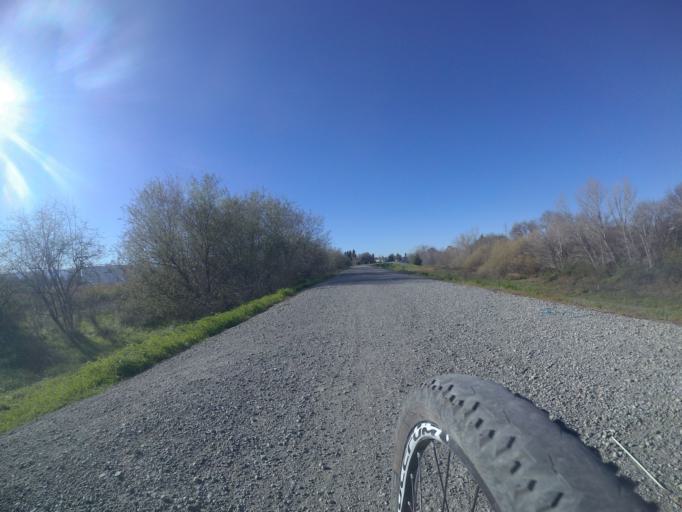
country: US
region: California
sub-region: Santa Clara County
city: Santa Clara
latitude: 37.3767
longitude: -121.9346
